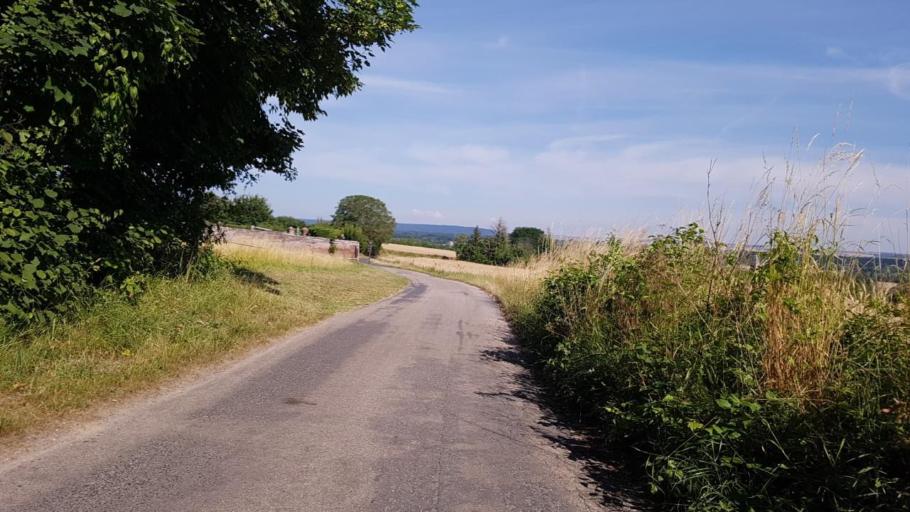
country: FR
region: Picardie
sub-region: Departement de l'Oise
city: Pontpoint
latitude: 49.2961
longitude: 2.6432
